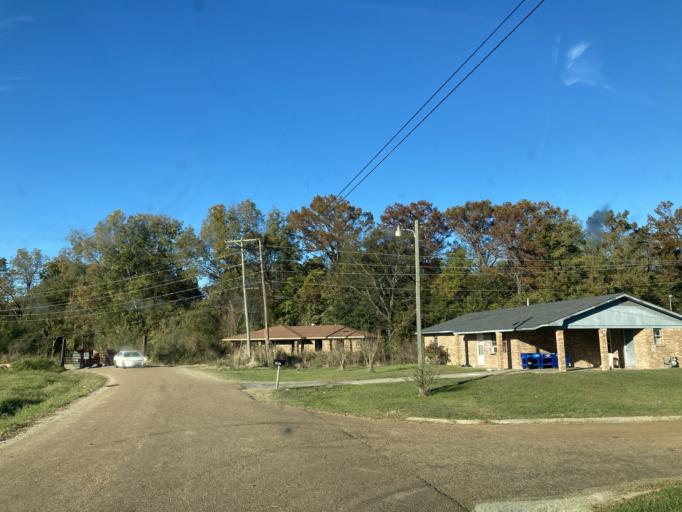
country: US
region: Mississippi
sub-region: Yazoo County
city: Yazoo City
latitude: 32.8822
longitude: -90.4197
